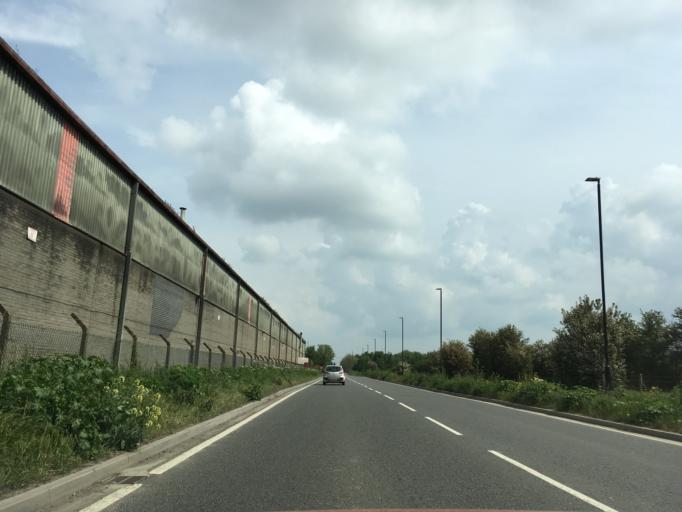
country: GB
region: England
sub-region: South Gloucestershire
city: Severn Beach
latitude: 51.5287
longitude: -2.6754
